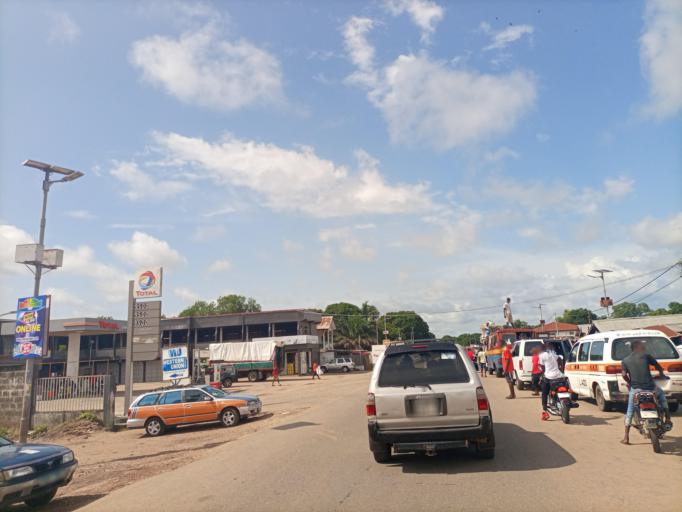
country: SL
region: Northern Province
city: Masoyila
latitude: 8.6058
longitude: -13.1795
